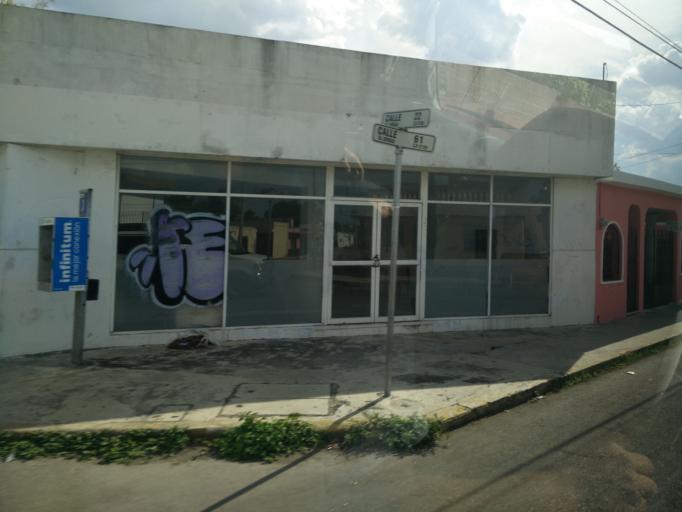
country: MX
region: Yucatan
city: Merida
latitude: 20.9649
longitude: -89.6006
